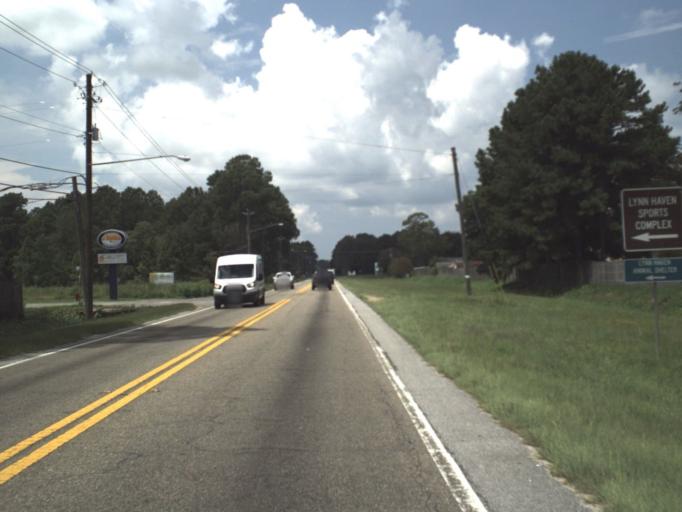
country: US
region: Florida
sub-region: Bay County
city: Hiland Park
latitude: 30.2333
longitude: -85.6148
